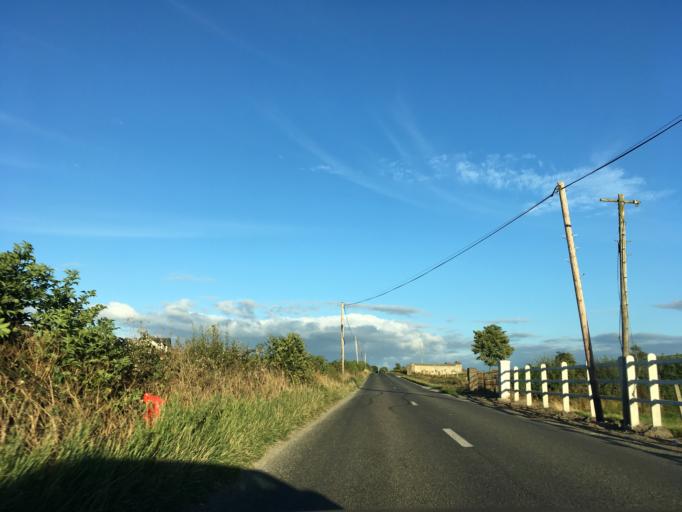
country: IE
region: Munster
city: Cashel
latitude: 52.4865
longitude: -7.9475
